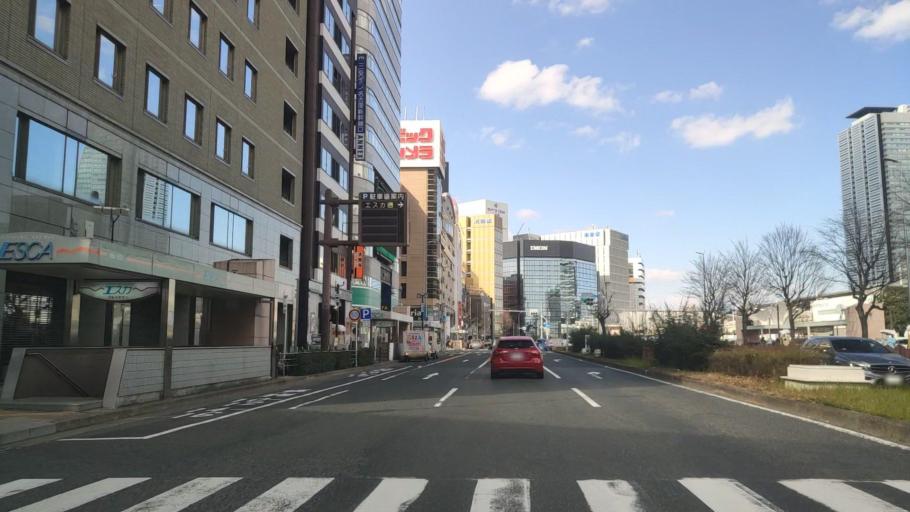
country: JP
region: Aichi
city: Nagoya-shi
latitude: 35.1693
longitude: 136.8805
